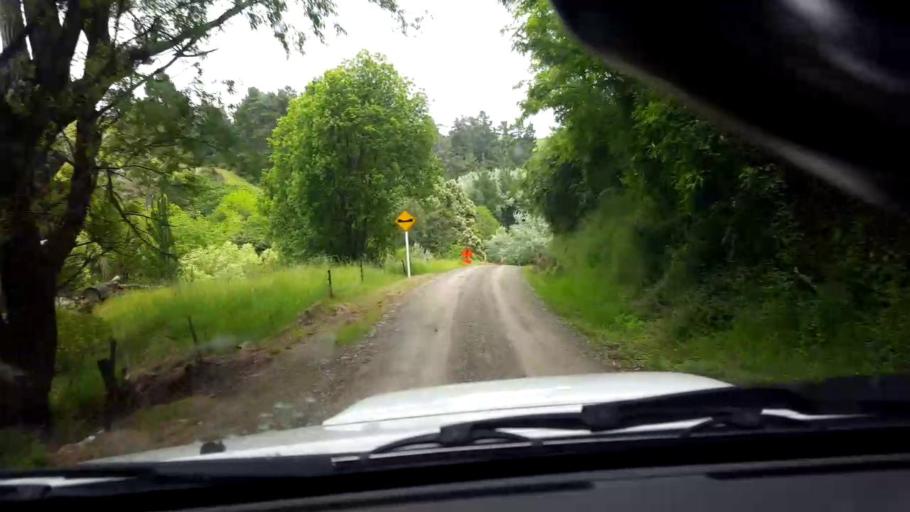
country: NZ
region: Gisborne
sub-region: Gisborne District
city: Gisborne
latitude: -38.3832
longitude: 177.6290
